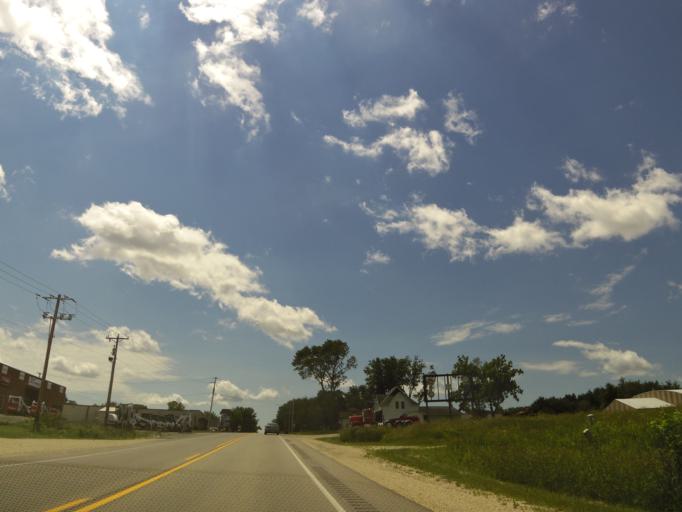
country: US
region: Iowa
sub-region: Fayette County
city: Oelwein
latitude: 42.6919
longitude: -91.9132
